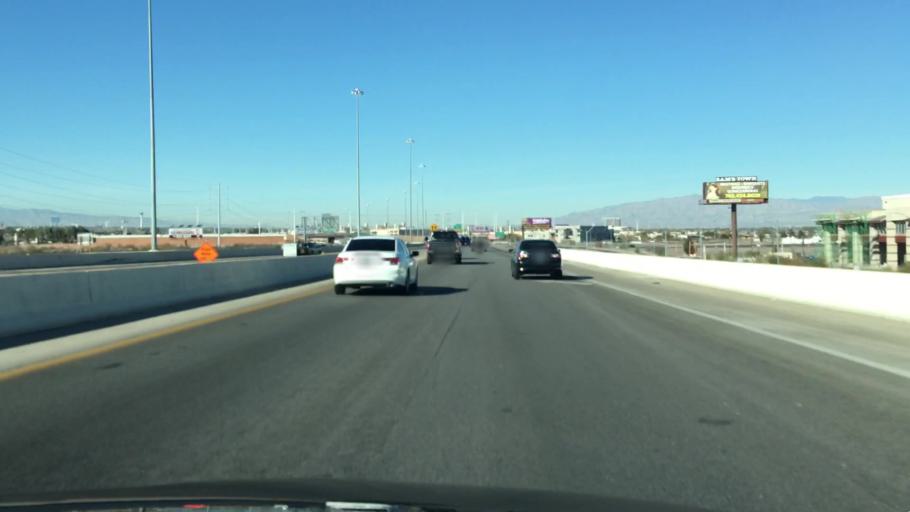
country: US
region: Nevada
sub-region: Clark County
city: Whitney
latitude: 36.0748
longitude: -115.0378
